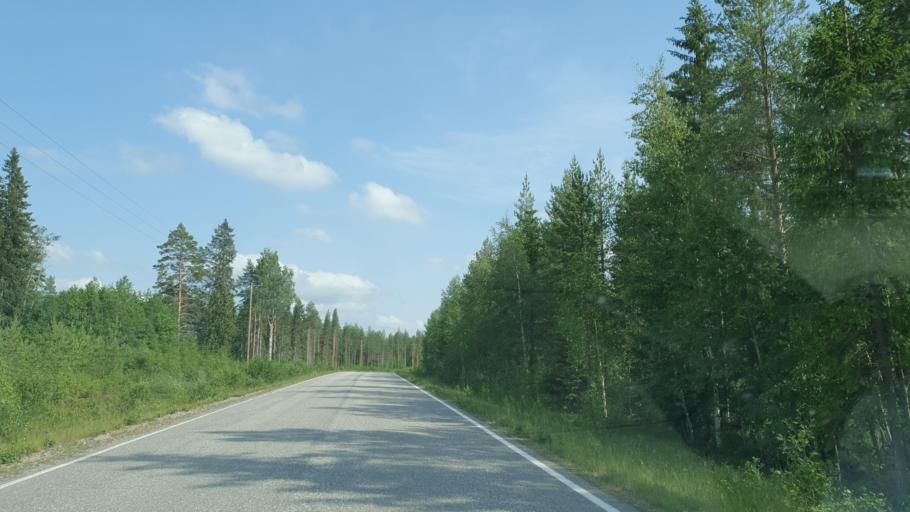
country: FI
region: Kainuu
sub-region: Kehys-Kainuu
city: Kuhmo
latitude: 64.0865
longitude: 29.8237
